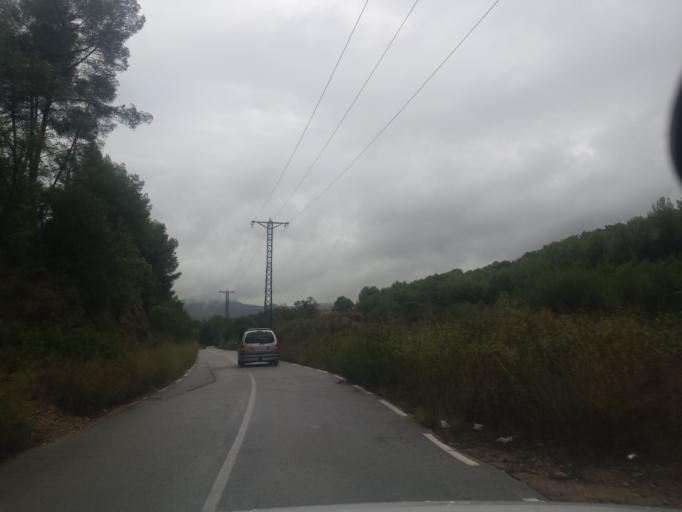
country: ES
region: Catalonia
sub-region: Provincia de Barcelona
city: Sant Andreu de la Barca
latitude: 41.4450
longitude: 1.9610
